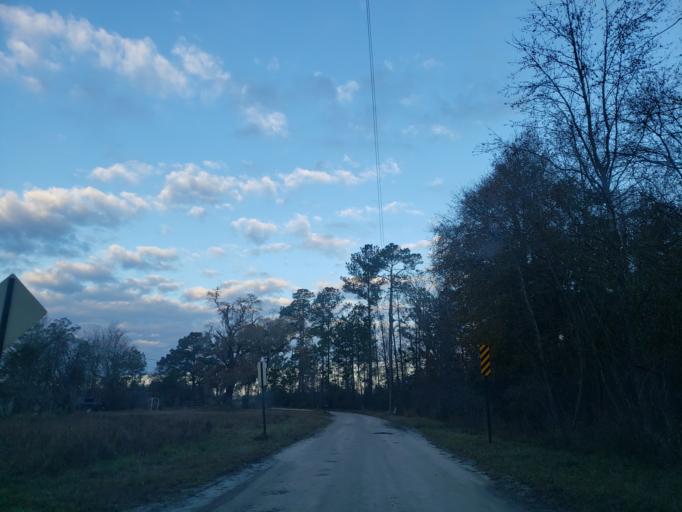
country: US
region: Georgia
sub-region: Chatham County
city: Bloomingdale
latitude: 32.1134
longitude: -81.3450
